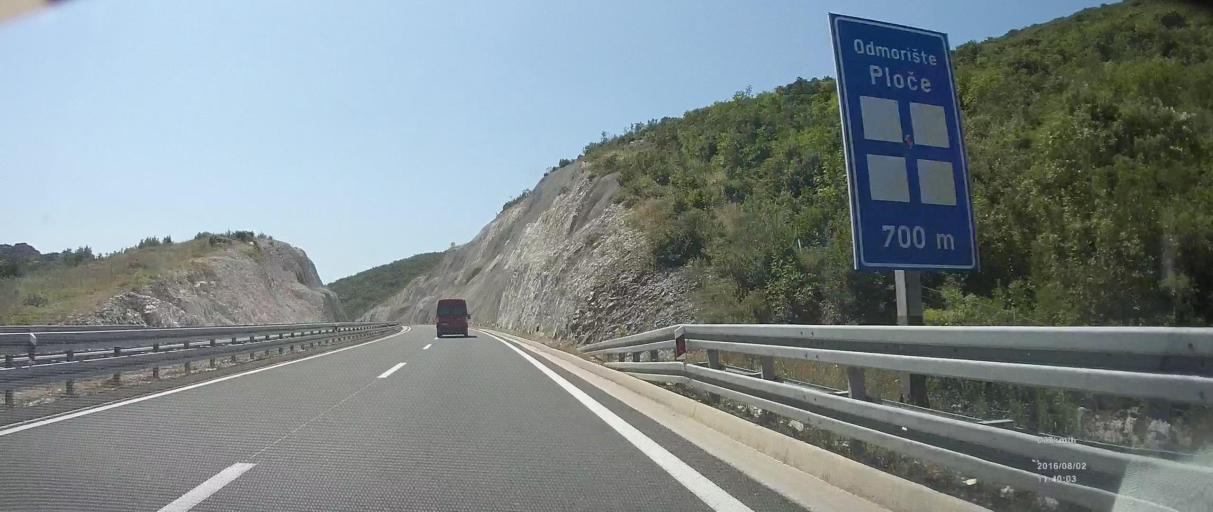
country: HR
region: Dubrovacko-Neretvanska
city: Komin
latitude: 43.0795
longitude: 17.4890
